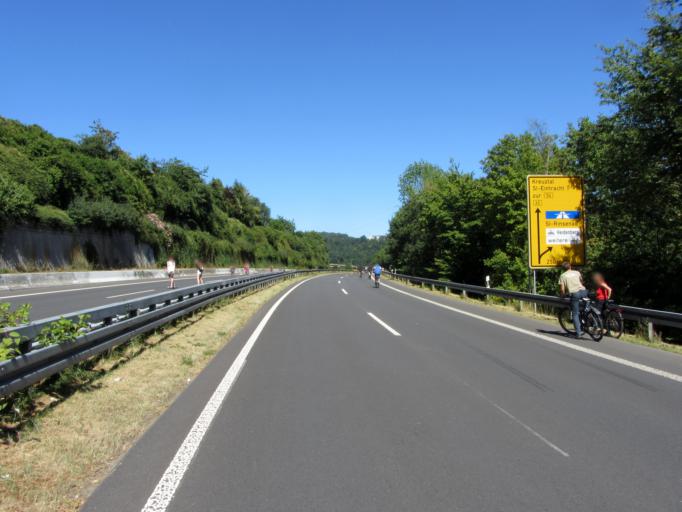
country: DE
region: North Rhine-Westphalia
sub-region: Regierungsbezirk Arnsberg
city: Siegen
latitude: 50.8546
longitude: 7.9969
